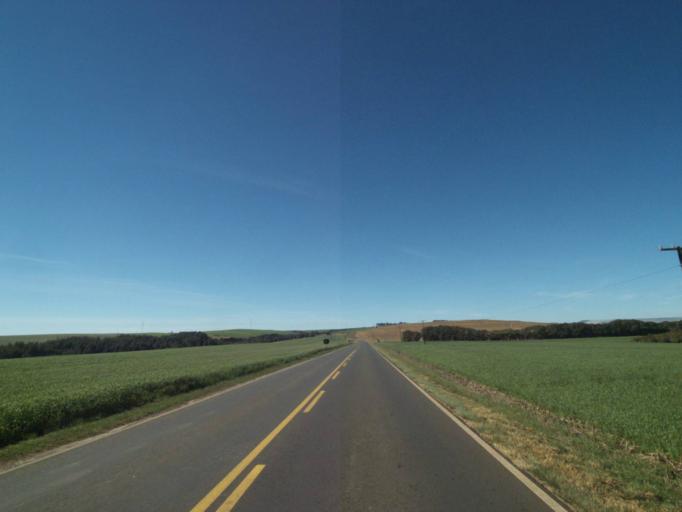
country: BR
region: Parana
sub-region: Tibagi
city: Tibagi
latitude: -24.5693
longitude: -50.2832
